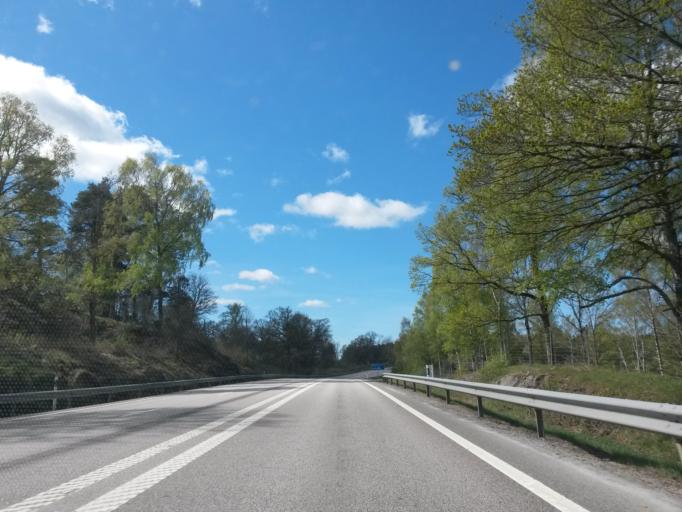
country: SE
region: Vaestra Goetaland
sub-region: Vargarda Kommun
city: Jonstorp
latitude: 58.0075
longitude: 12.7655
